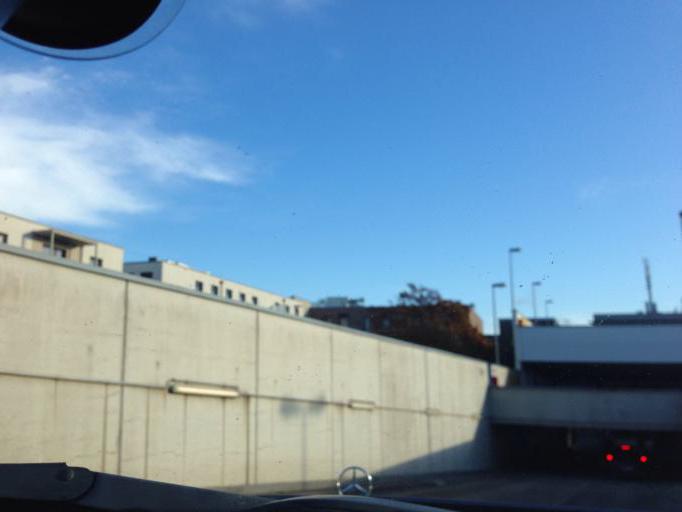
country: DE
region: Hamburg
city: Farmsen-Berne
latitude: 53.5878
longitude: 10.1263
